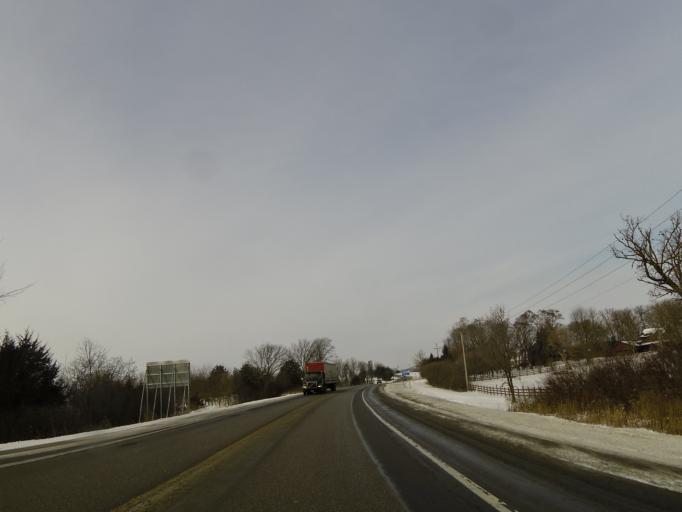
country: US
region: Minnesota
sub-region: Hennepin County
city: Saint Bonifacius
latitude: 44.8918
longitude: -93.7085
